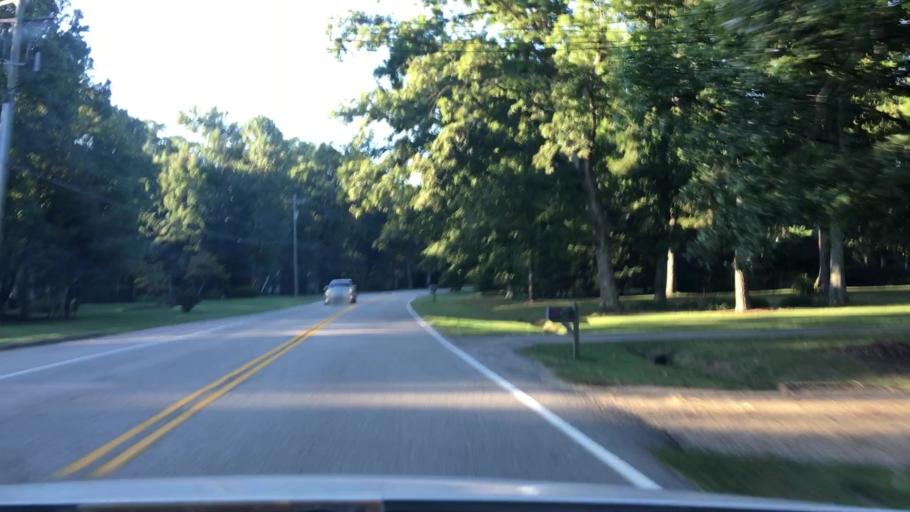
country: US
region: Virginia
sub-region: Chesterfield County
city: Bon Air
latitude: 37.5281
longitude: -77.6412
